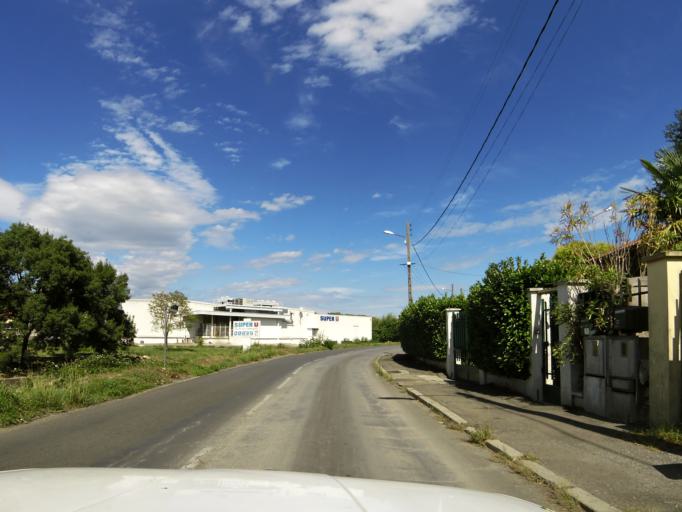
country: FR
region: Languedoc-Roussillon
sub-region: Departement du Gard
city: Ales
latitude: 44.1398
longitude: 4.0901
